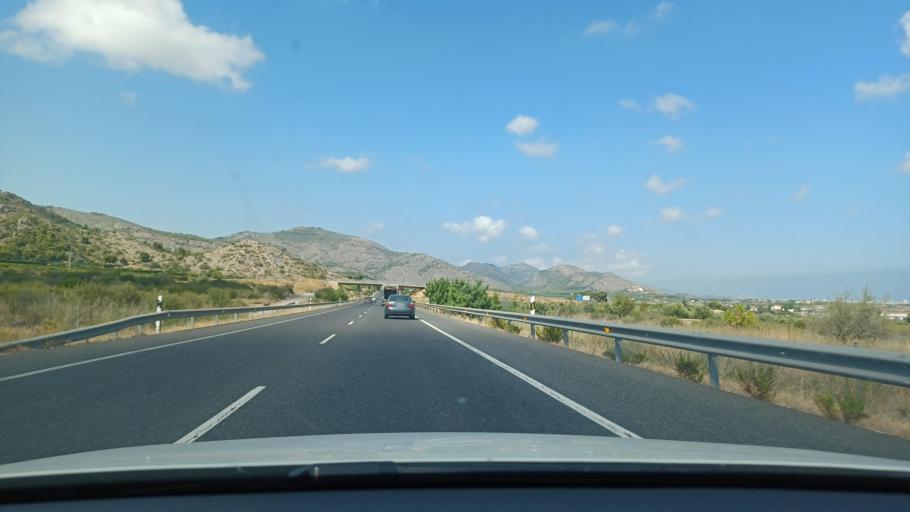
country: ES
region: Valencia
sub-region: Provincia de Castello
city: Borriol
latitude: 40.0203
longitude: -0.0411
